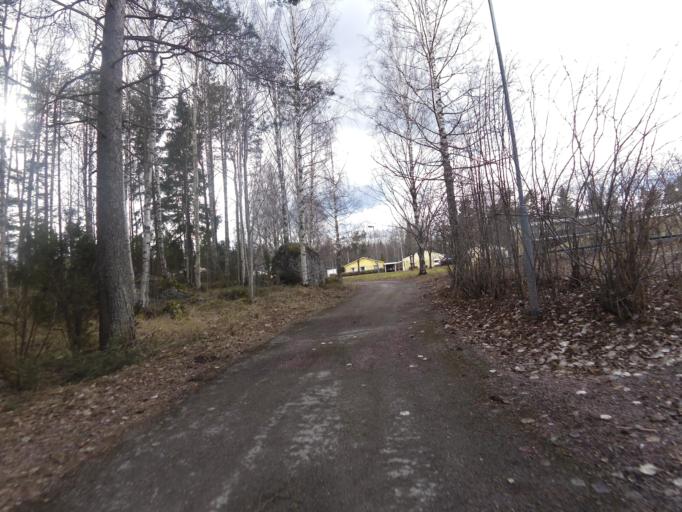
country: SE
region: Gaevleborg
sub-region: Gavle Kommun
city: Gavle
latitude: 60.6975
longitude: 17.1113
